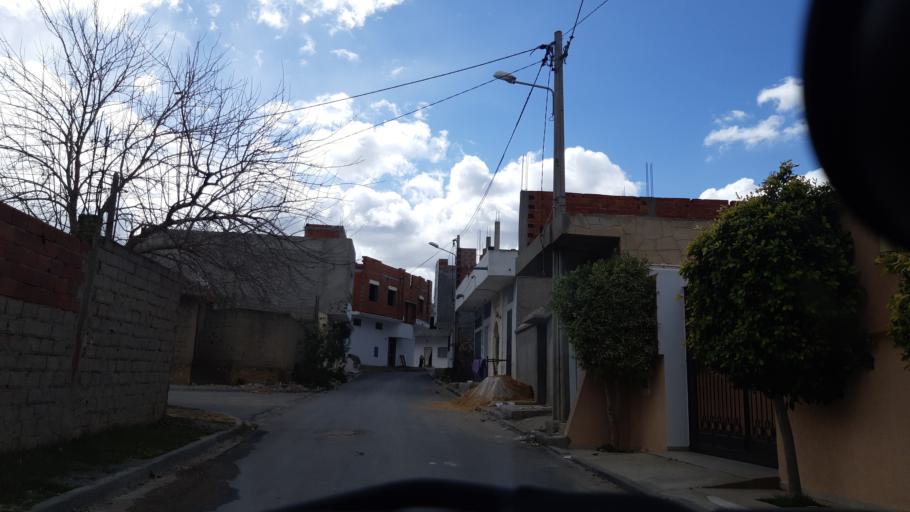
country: TN
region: Susah
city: Akouda
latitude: 35.8689
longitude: 10.5191
